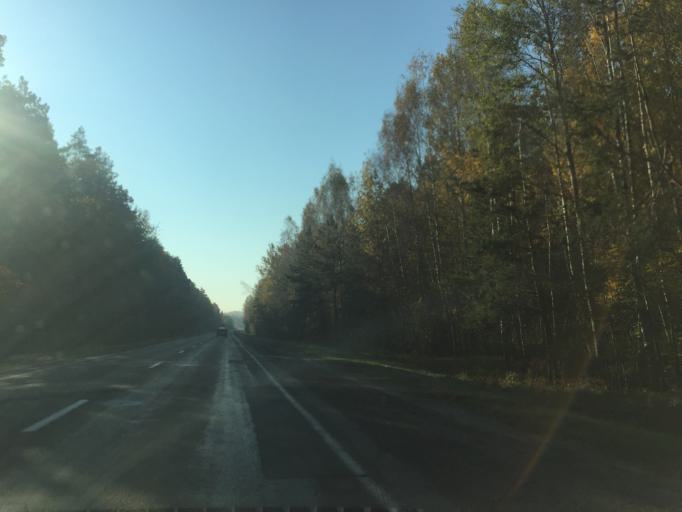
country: BY
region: Gomel
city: Kastsyukowka
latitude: 52.4291
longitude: 30.8275
